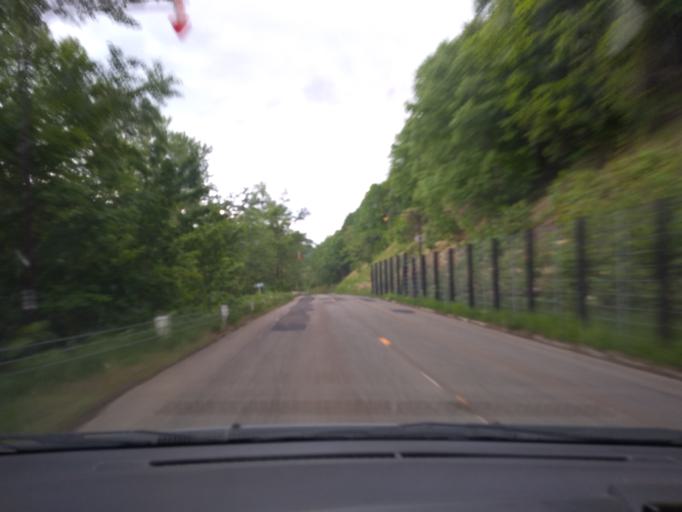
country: JP
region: Hokkaido
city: Shimo-furano
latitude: 43.1409
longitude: 142.4777
